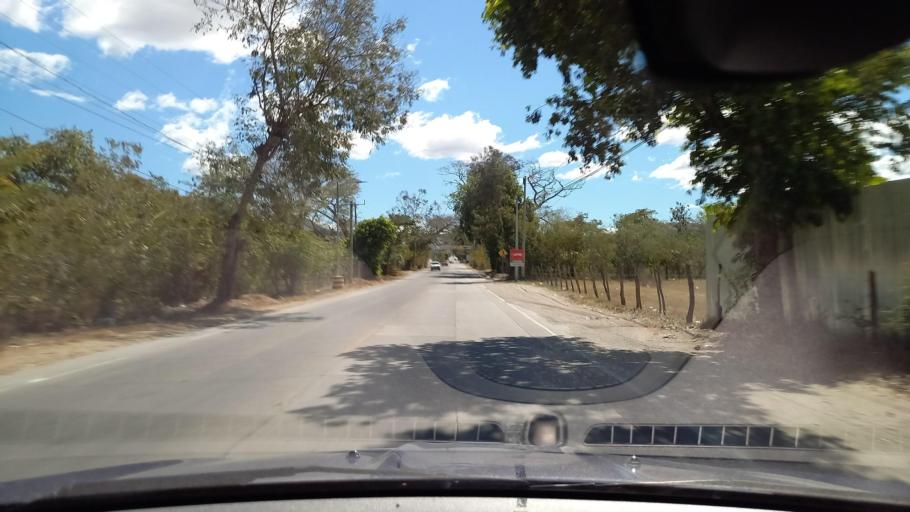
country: SV
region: Santa Ana
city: Metapan
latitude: 14.3402
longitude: -89.4508
